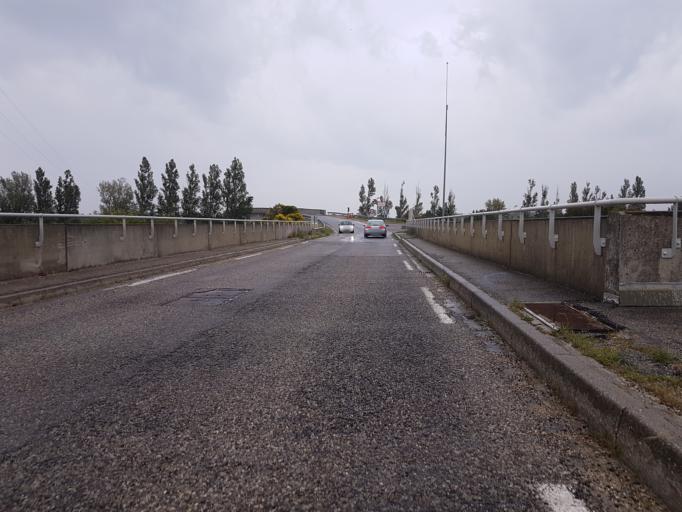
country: FR
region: Languedoc-Roussillon
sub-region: Departement du Gard
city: Villeneuve-les-Avignon
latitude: 43.9957
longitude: 4.8178
